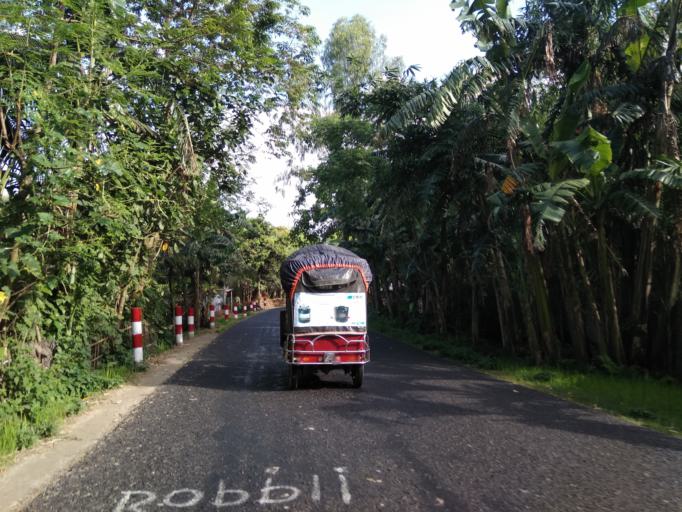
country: BD
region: Rangpur Division
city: Rangpur
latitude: 25.8407
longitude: 89.1136
